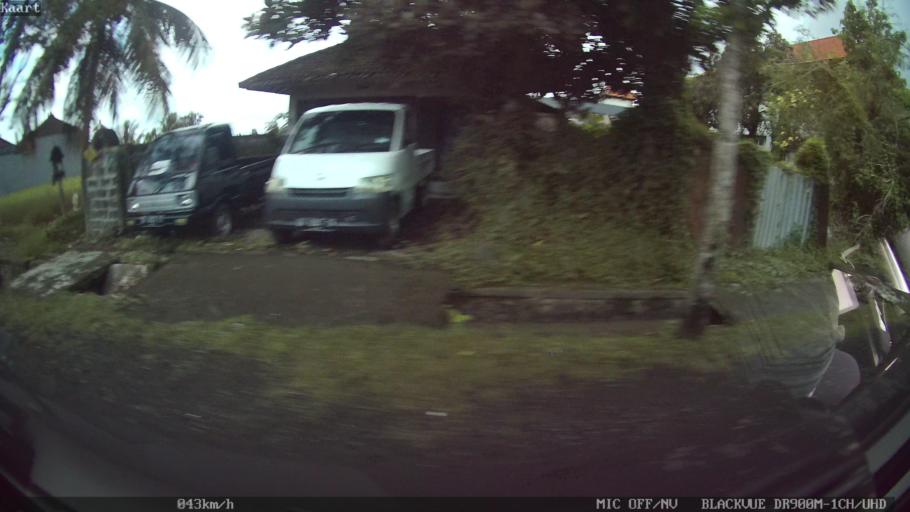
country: ID
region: Bali
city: Banjar Keraman
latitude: -8.5346
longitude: 115.2139
